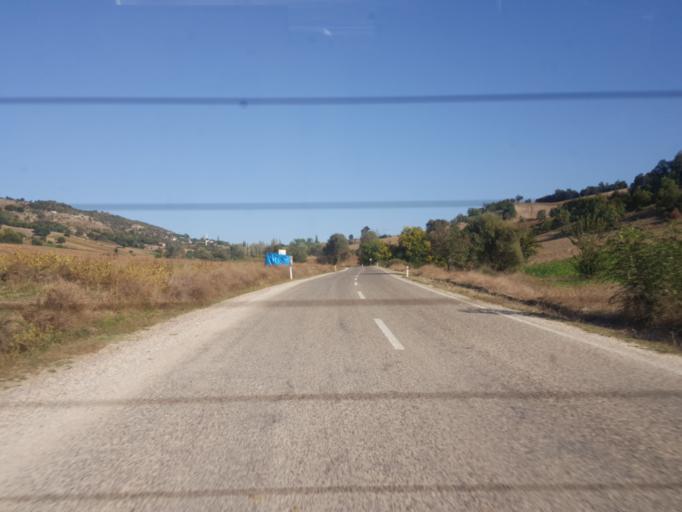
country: TR
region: Amasya
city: Tasova
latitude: 40.7180
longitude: 36.3082
